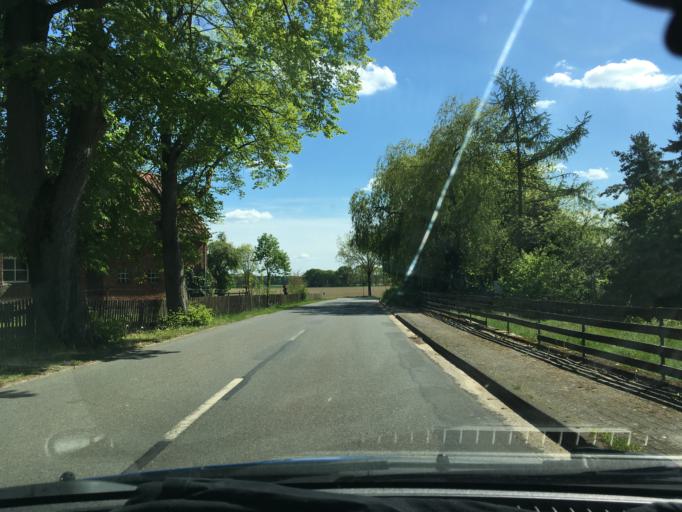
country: DE
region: Lower Saxony
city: Zernien
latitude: 53.0331
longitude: 10.8879
